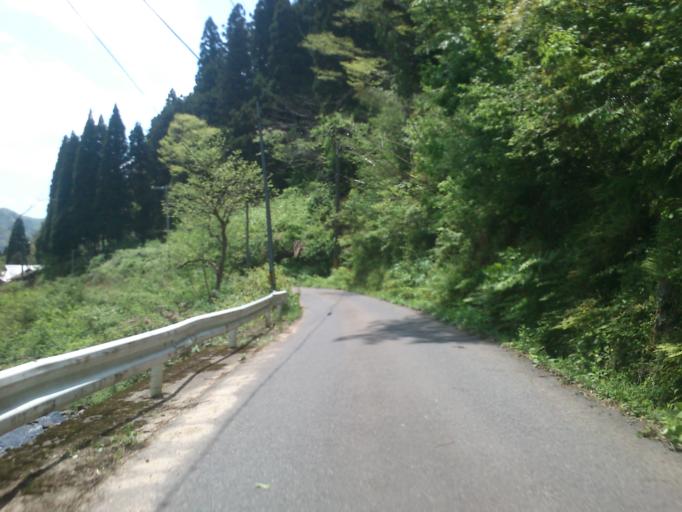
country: JP
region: Kyoto
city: Miyazu
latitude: 35.6702
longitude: 135.1603
